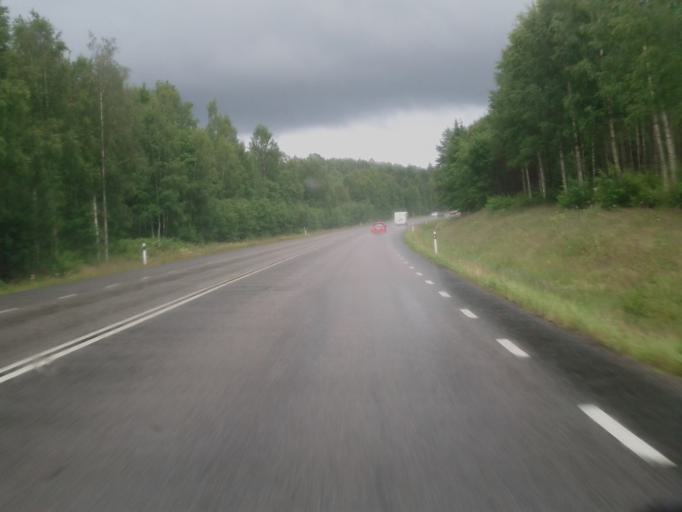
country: SE
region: Dalarna
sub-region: Rattviks Kommun
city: Vikarbyn
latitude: 60.9070
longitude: 15.0645
